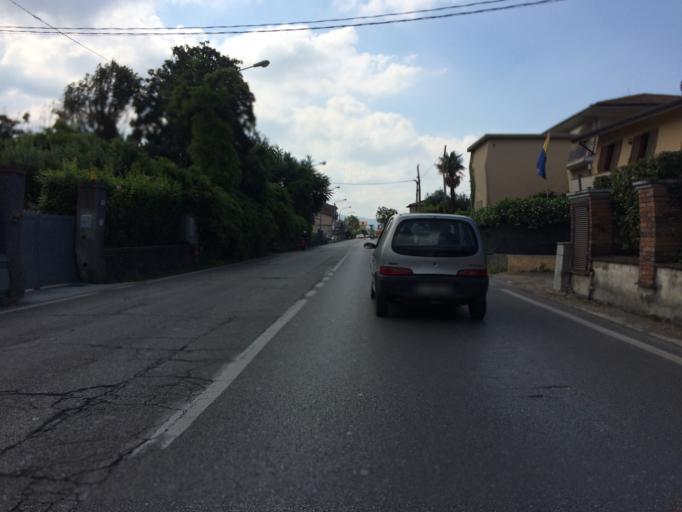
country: IT
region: Tuscany
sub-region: Provincia di Lucca
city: Ripa-Pozzi-Querceta-Ponterosso
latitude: 43.9711
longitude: 10.2077
